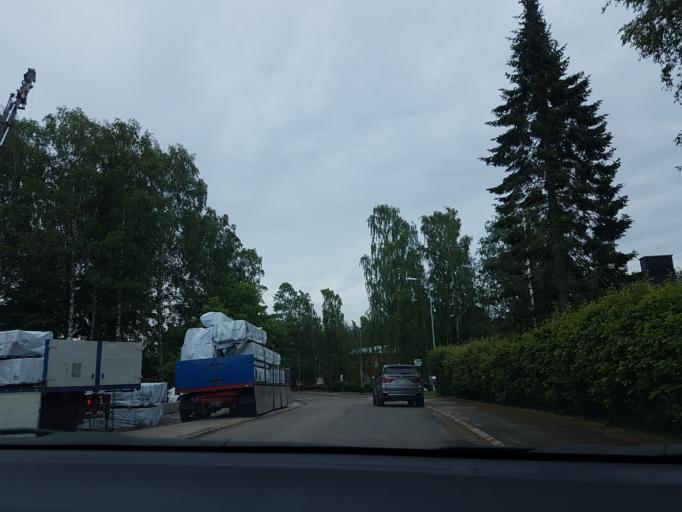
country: FI
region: Uusimaa
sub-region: Helsinki
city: Vantaa
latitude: 60.2099
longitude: 25.1259
